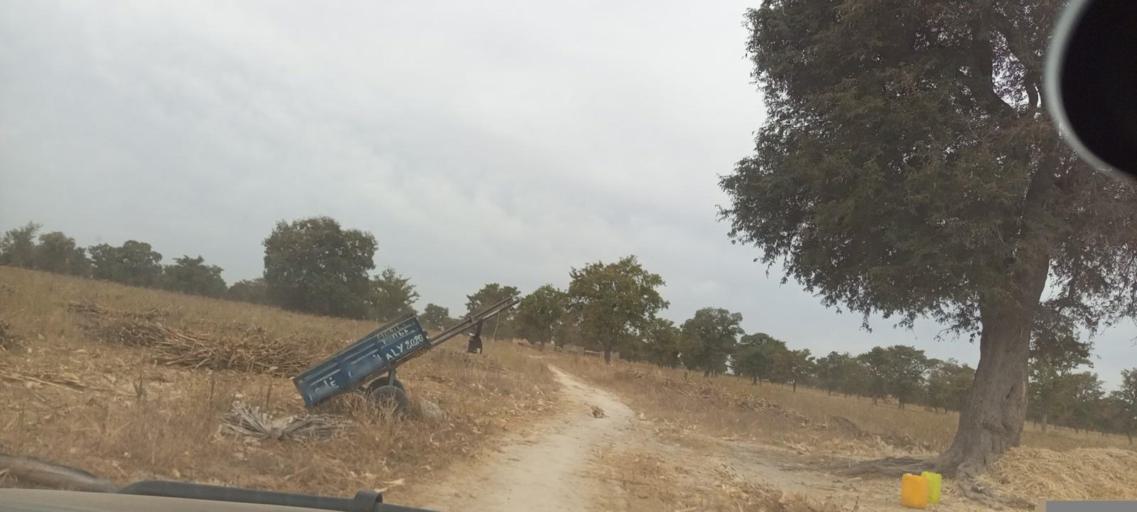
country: ML
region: Koulikoro
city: Kati
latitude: 12.7456
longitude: -8.3347
